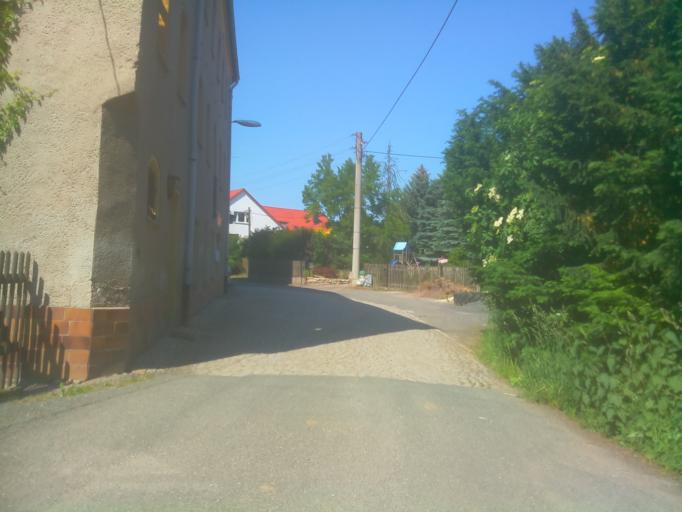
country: DE
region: Thuringia
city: Bodelwitz
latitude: 50.7086
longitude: 11.6141
